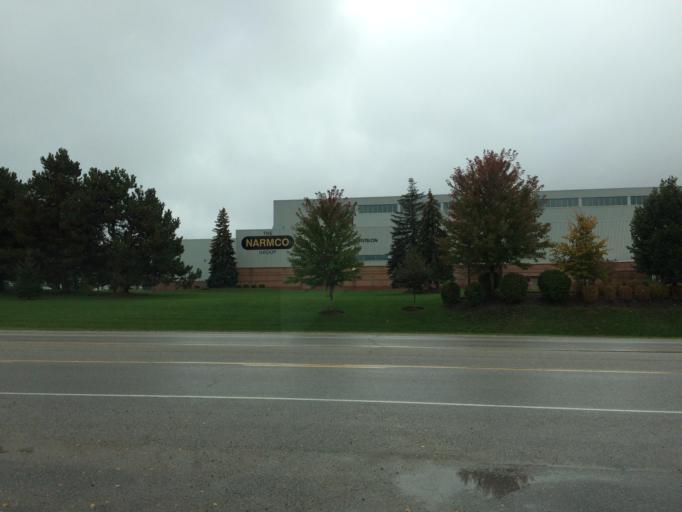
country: CA
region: Ontario
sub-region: Wellington County
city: Guelph
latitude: 43.5339
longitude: -80.3077
